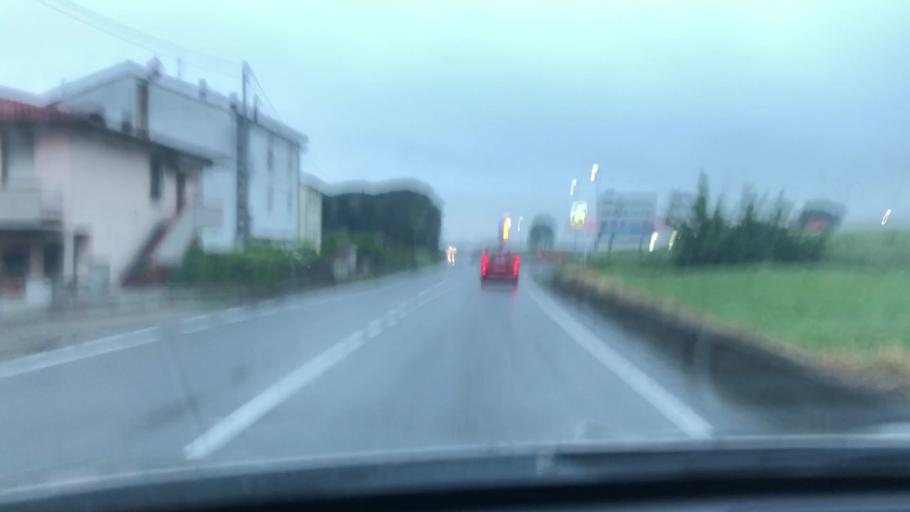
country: IT
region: Tuscany
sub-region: Province of Pisa
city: Val di Cava
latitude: 43.6403
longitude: 10.6505
